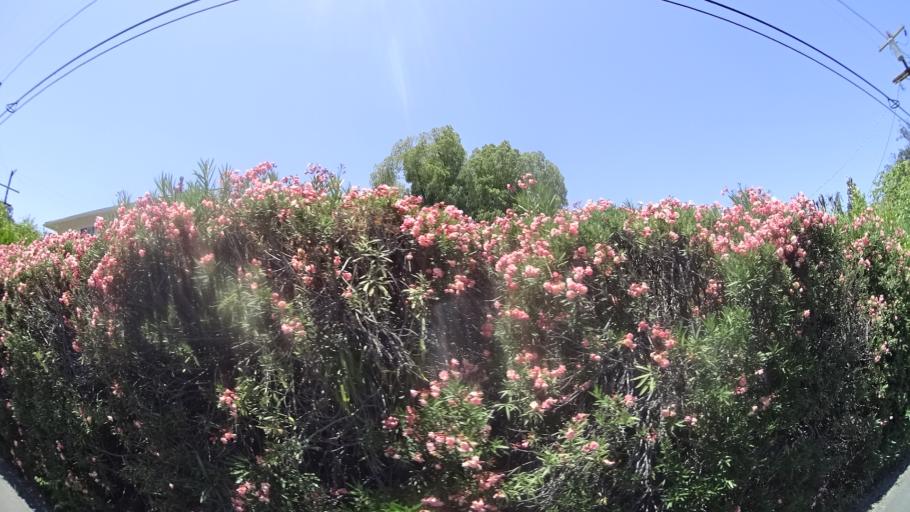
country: US
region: California
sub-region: Los Angeles County
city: Sherman Oaks
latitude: 34.1532
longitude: -118.4793
